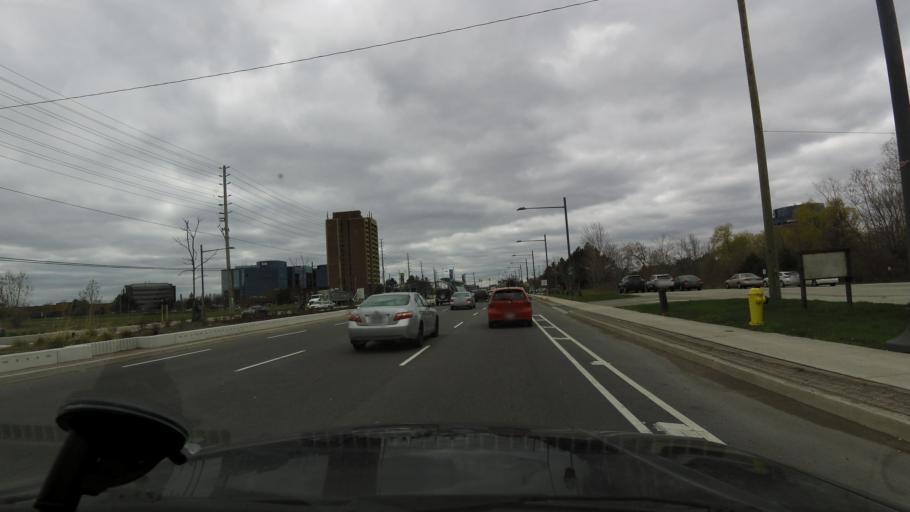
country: CA
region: Ontario
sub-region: York
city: Richmond Hill
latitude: 43.8491
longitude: -79.3622
